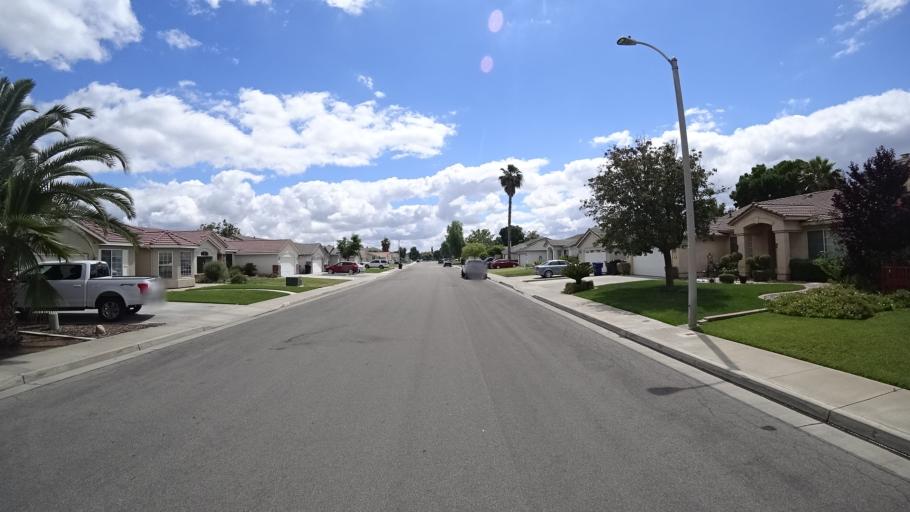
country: US
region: California
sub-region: Kings County
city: Lucerne
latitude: 36.3600
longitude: -119.6581
